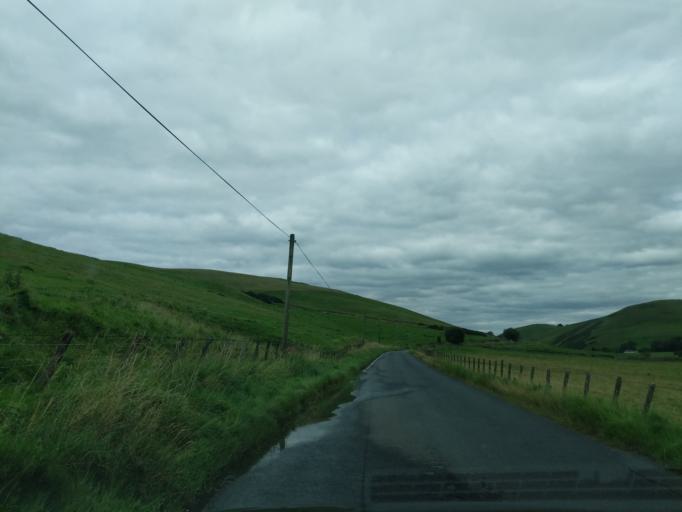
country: GB
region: Scotland
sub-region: The Scottish Borders
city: West Linton
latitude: 55.6827
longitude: -3.3342
